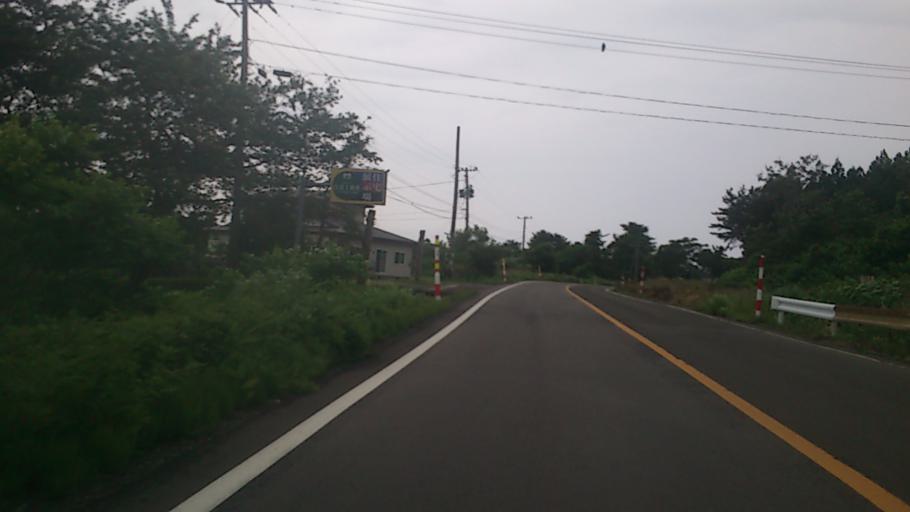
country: JP
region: Akita
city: Noshiromachi
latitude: 40.3848
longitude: 139.9924
